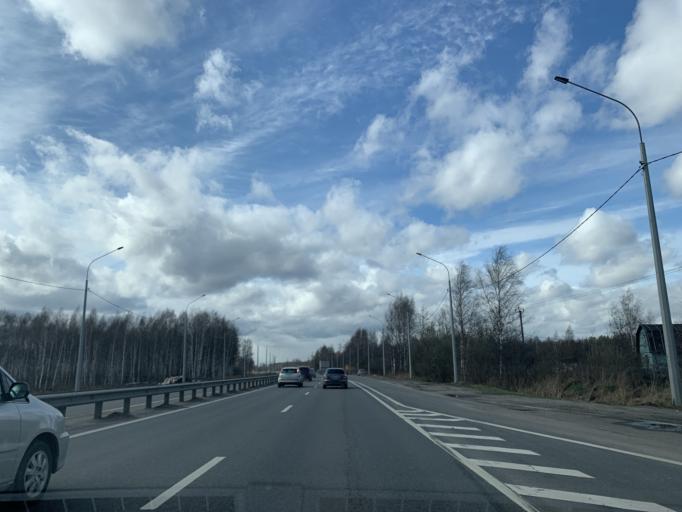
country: RU
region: Jaroslavl
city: Yaroslavl
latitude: 57.6748
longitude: 39.9396
